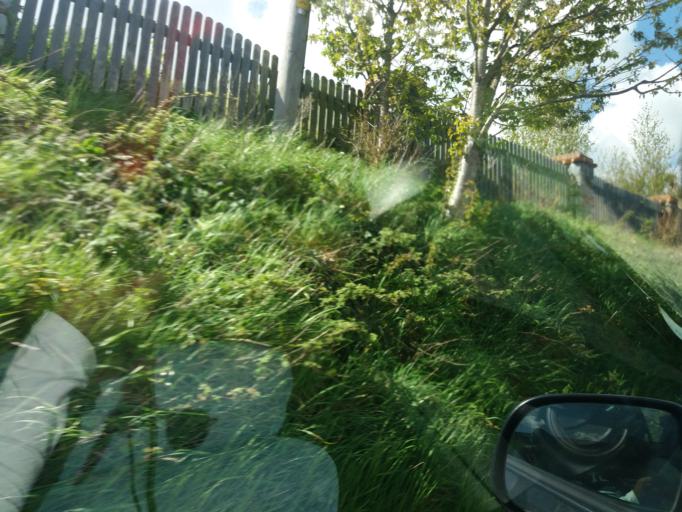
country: IE
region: Munster
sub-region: Waterford
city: Dunmore East
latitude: 52.2439
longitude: -6.9563
